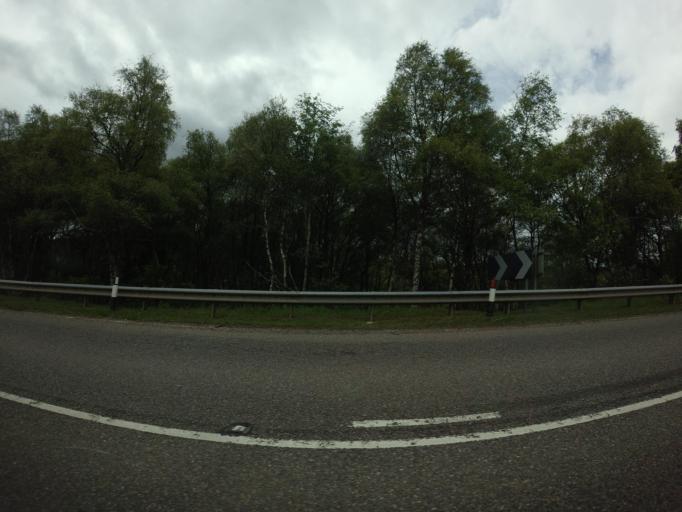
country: GB
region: Scotland
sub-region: Highland
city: Dingwall
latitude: 57.6870
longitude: -4.6983
